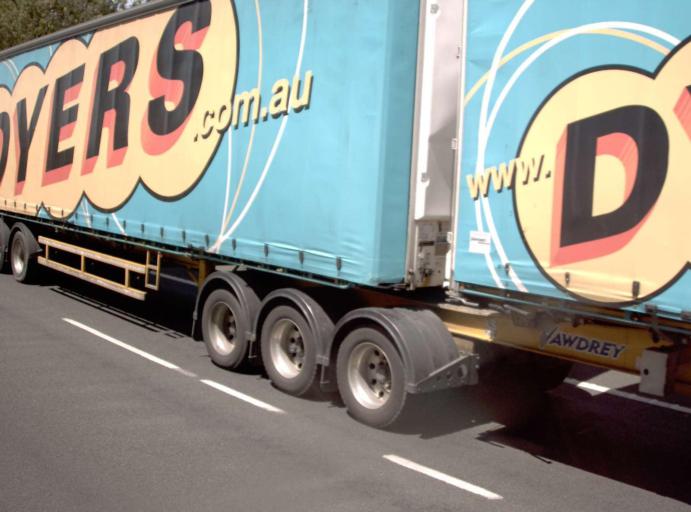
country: AU
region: Victoria
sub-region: Latrobe
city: Traralgon
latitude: -38.1636
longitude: 146.7026
